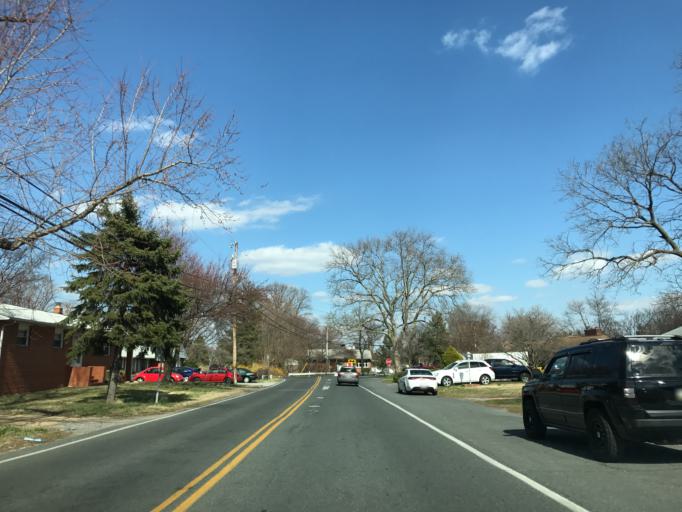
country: US
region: Maryland
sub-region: Anne Arundel County
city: Riviera Beach
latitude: 39.1627
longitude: -76.5124
